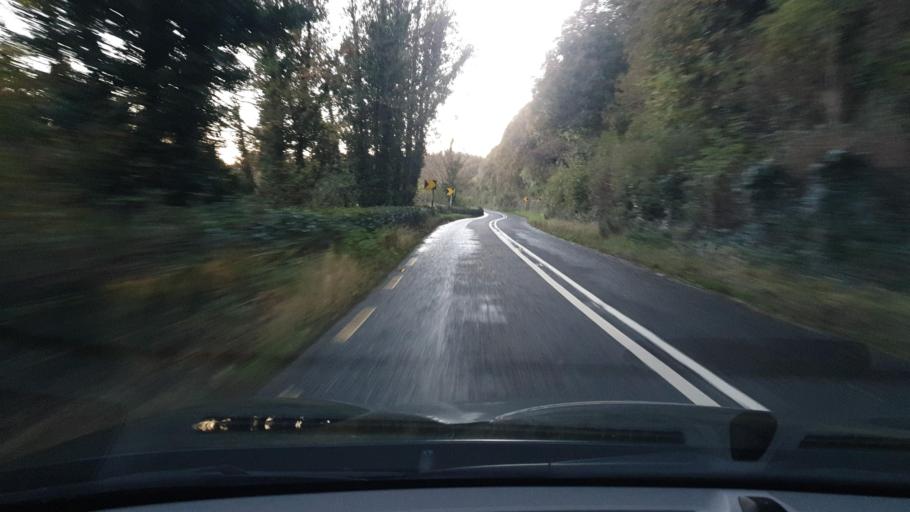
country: IE
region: Leinster
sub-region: Lu
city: Tullyallen
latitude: 53.7261
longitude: -6.4209
